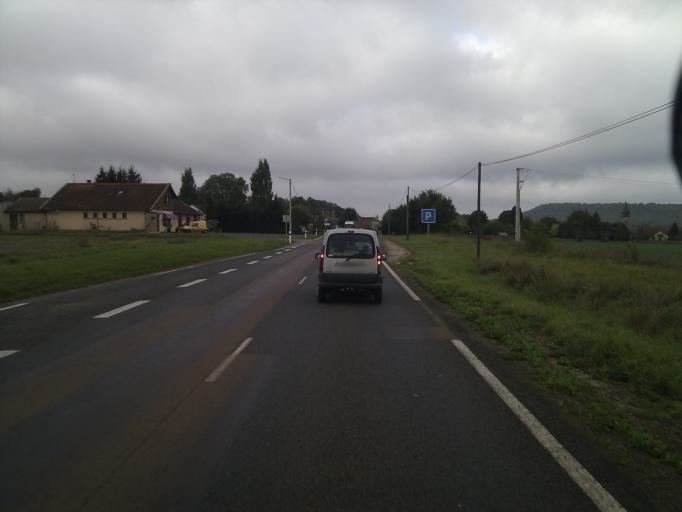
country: FR
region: Lorraine
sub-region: Departement des Vosges
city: Liffol-le-Grand
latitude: 48.2877
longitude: 5.4994
